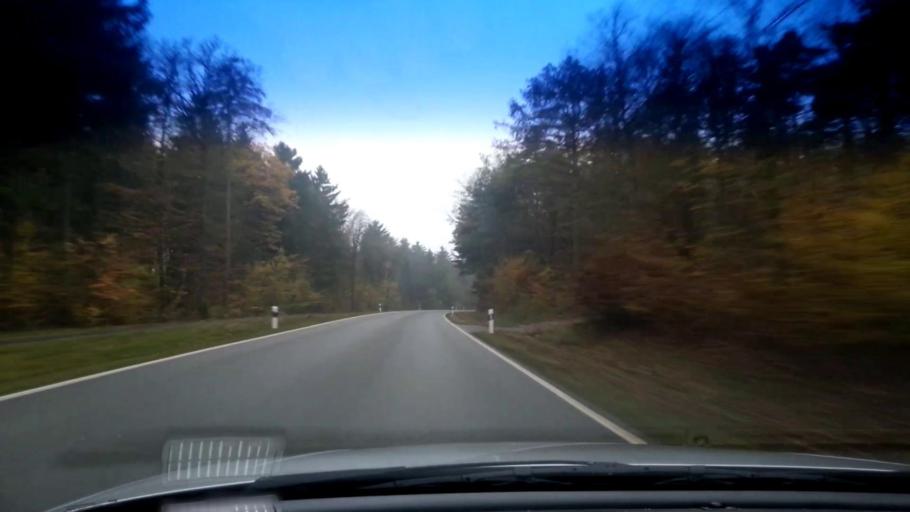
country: DE
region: Bavaria
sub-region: Upper Franconia
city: Litzendorf
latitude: 49.9308
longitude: 10.9917
